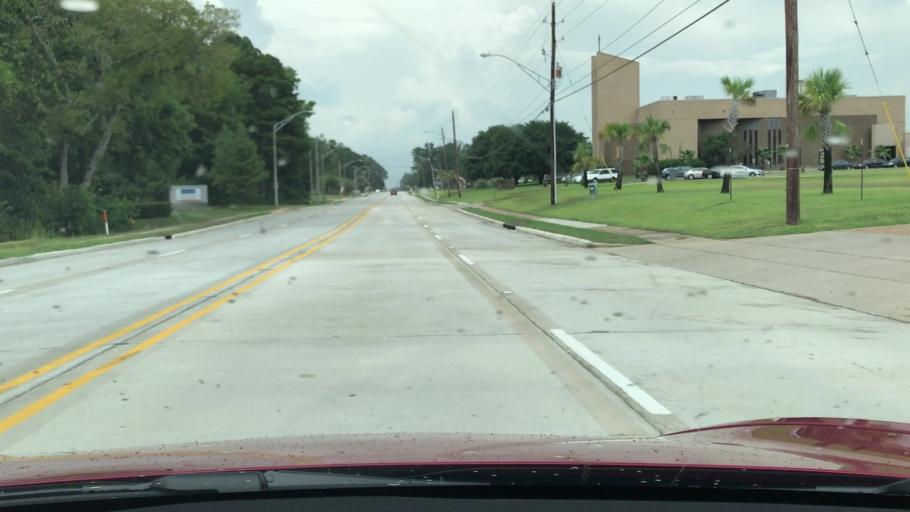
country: US
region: Louisiana
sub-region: Bossier Parish
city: Bossier City
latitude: 32.4025
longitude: -93.7633
